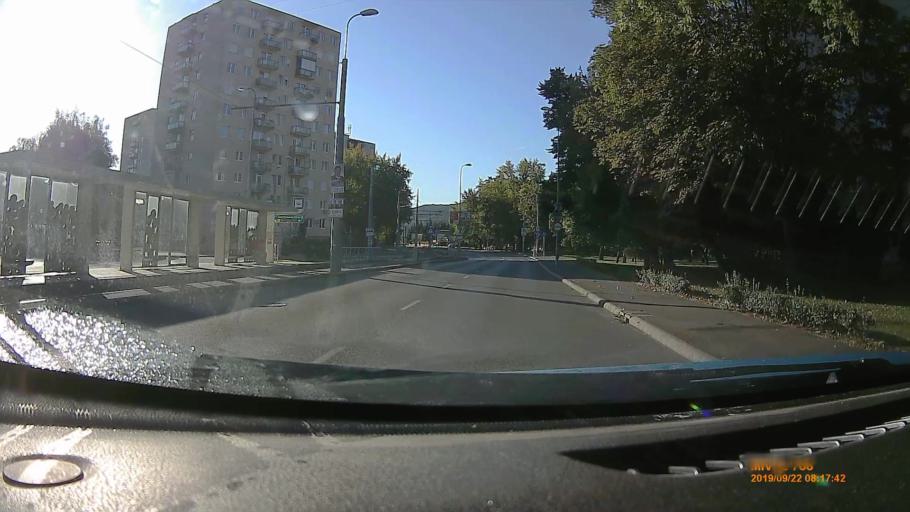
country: HU
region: Borsod-Abauj-Zemplen
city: Sajobabony
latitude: 48.1089
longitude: 20.6757
